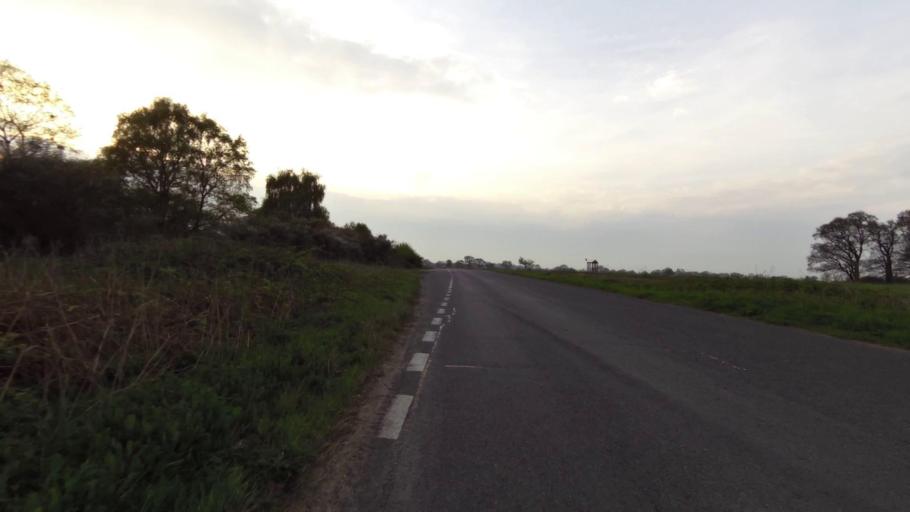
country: GB
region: England
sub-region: Suffolk
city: Shotley Gate
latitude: 52.0145
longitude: 1.2680
